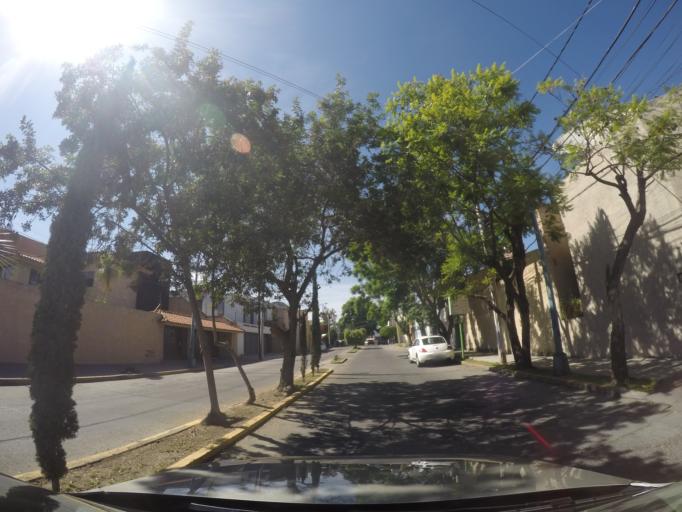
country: MX
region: San Luis Potosi
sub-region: San Luis Potosi
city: San Luis Potosi
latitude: 22.1507
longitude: -101.0122
